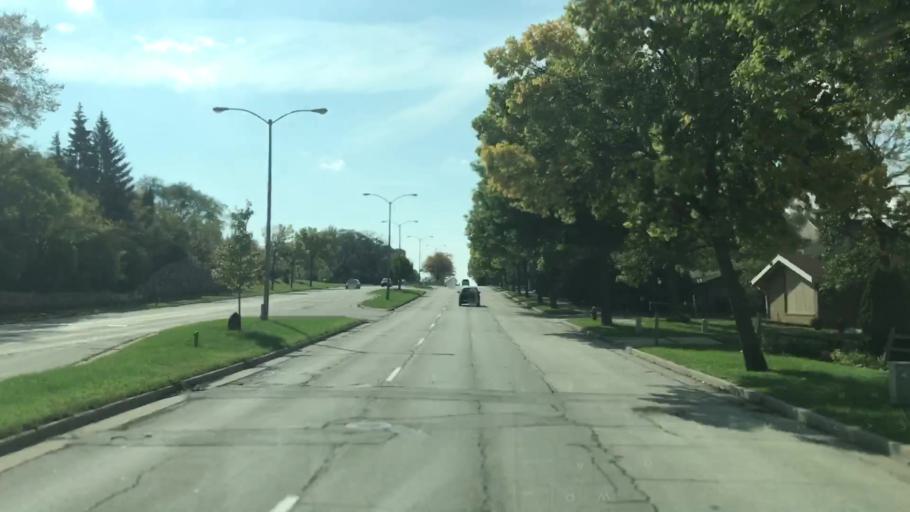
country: US
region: Wisconsin
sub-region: Waukesha County
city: Butler
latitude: 43.1668
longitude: -88.0445
